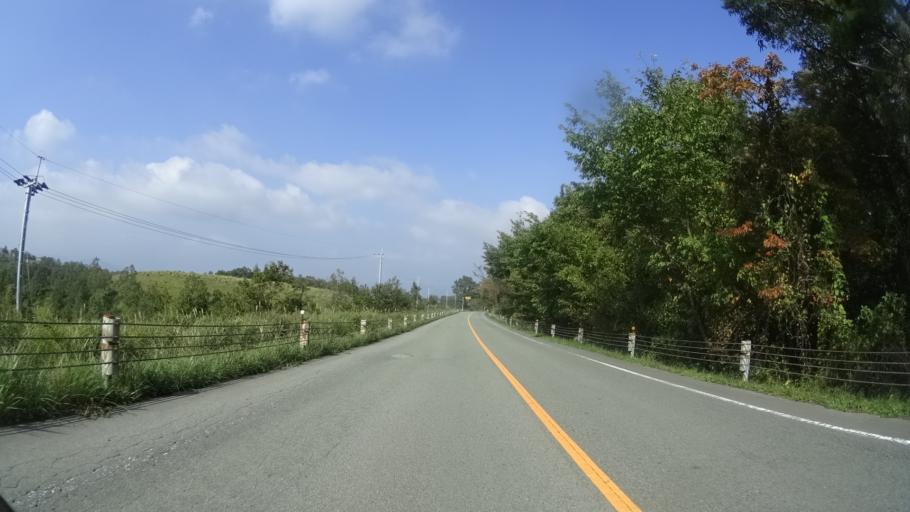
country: JP
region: Kumamoto
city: Aso
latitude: 33.0331
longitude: 131.0648
